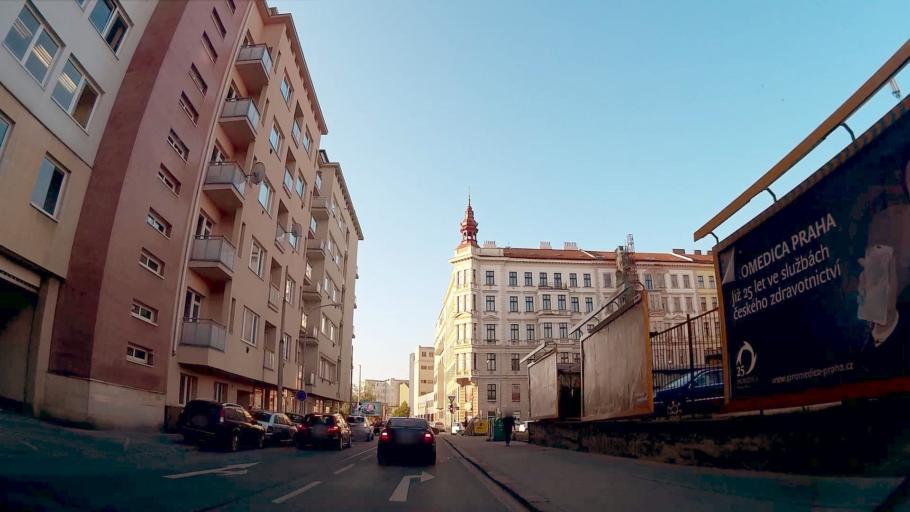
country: CZ
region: South Moravian
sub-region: Mesto Brno
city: Brno
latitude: 49.1991
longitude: 16.6150
